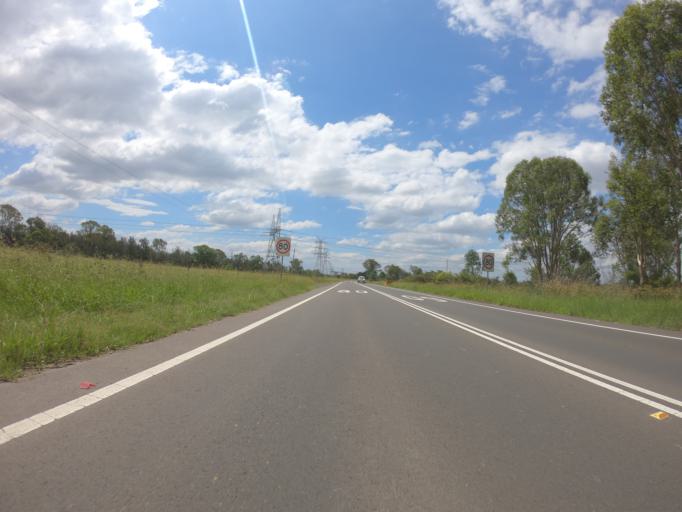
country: AU
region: New South Wales
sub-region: Penrith Municipality
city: Kingswood Park
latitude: -33.8151
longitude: 150.7601
